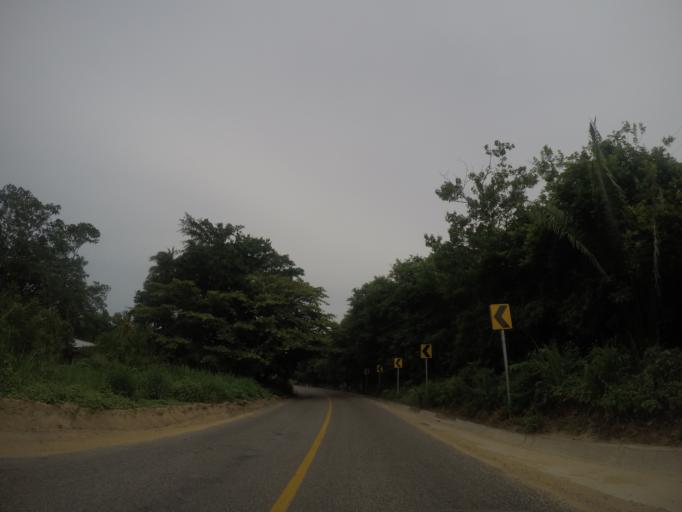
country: MX
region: Oaxaca
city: San Pedro Mixtepec
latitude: 15.9511
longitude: -97.1928
